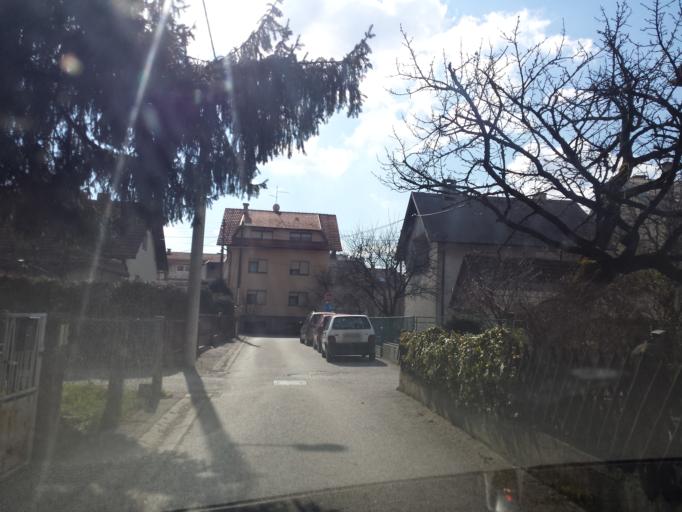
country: HR
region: Grad Zagreb
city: Stenjevec
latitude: 45.8100
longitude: 15.8976
